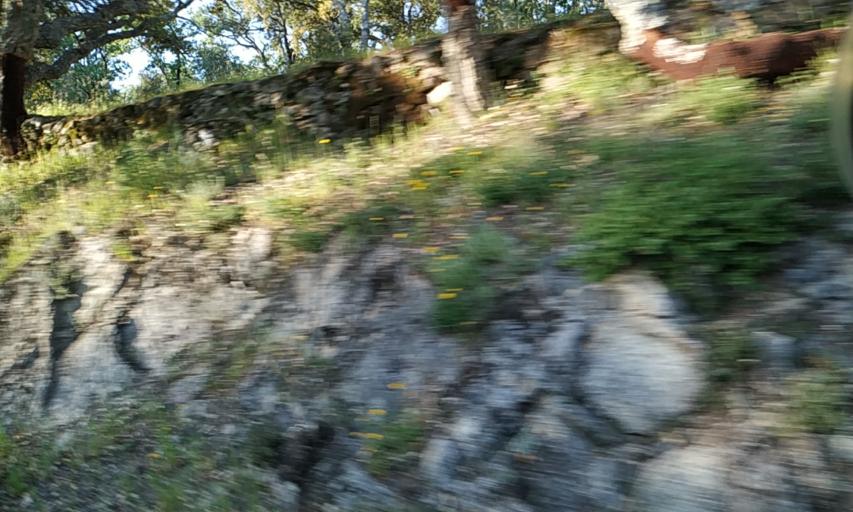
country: PT
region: Portalegre
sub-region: Portalegre
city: Portalegre
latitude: 39.3322
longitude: -7.4261
